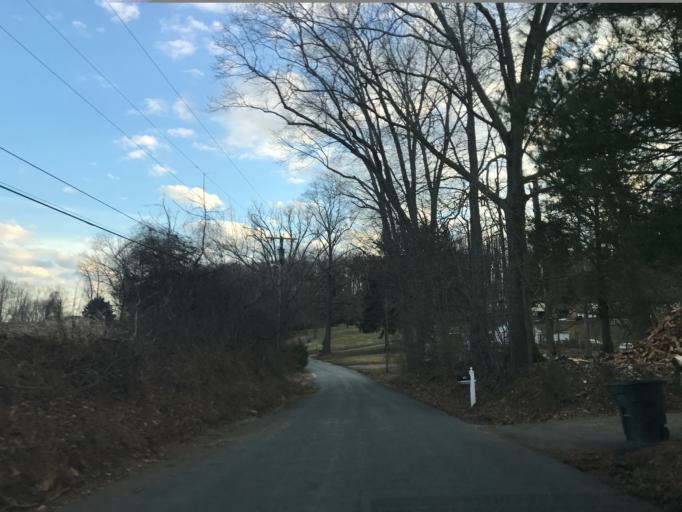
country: US
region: Maryland
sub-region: Harford County
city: Jarrettsville
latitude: 39.6204
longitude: -76.4211
